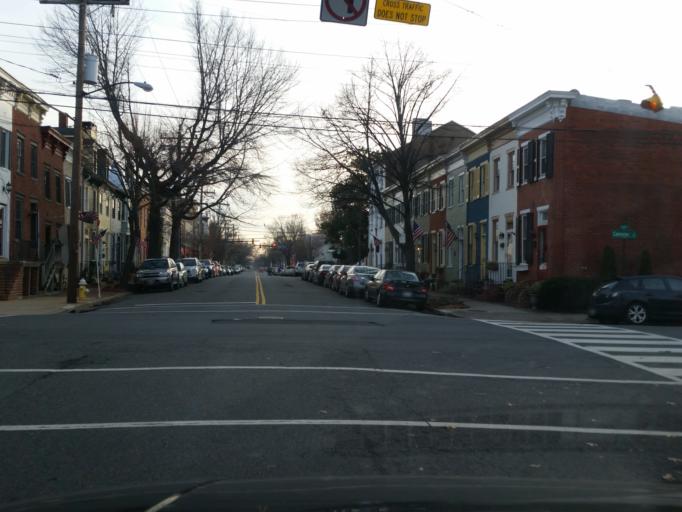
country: US
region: Virginia
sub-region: City of Alexandria
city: Alexandria
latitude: 38.8072
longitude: -77.0532
